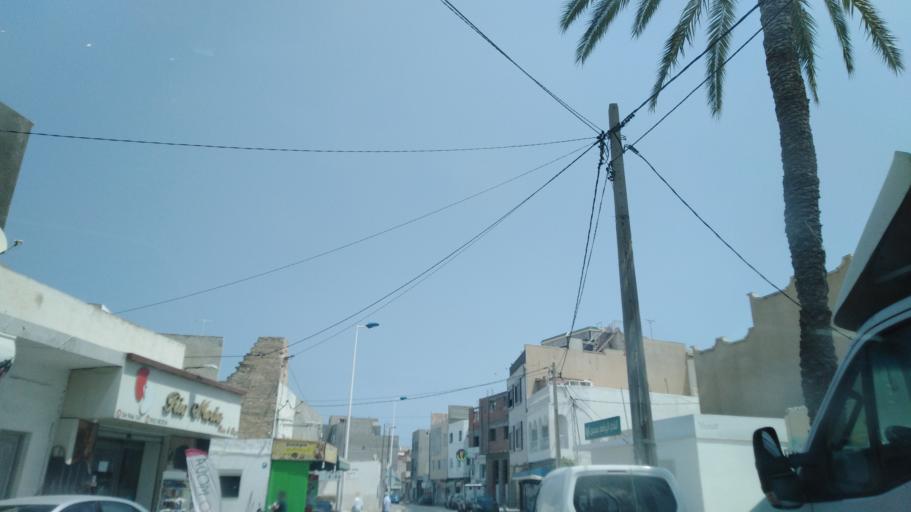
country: TN
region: Al Mahdiyah
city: Mahdia
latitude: 35.5140
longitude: 11.0420
